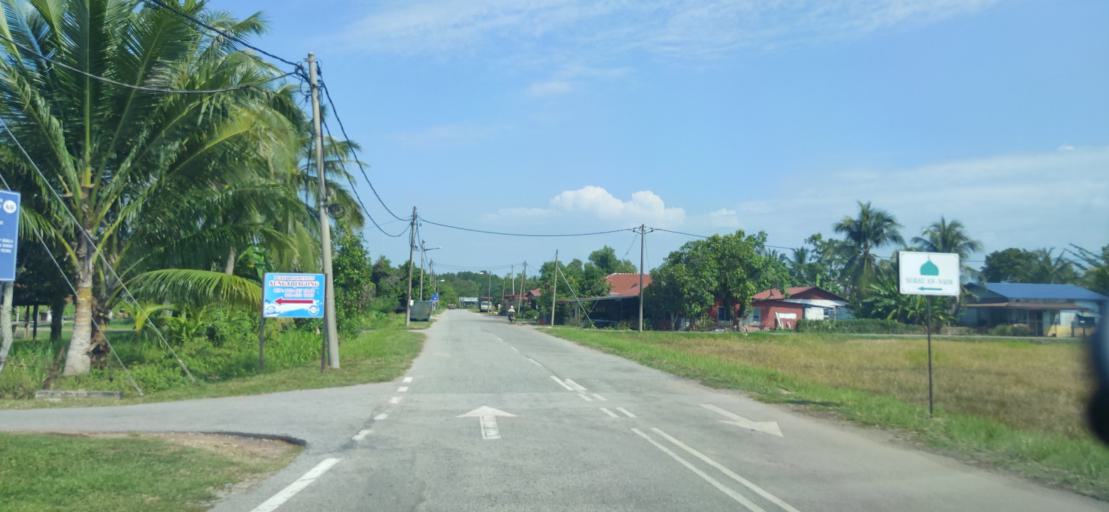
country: MY
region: Kedah
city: Sungai Petani
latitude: 5.6614
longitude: 100.4625
